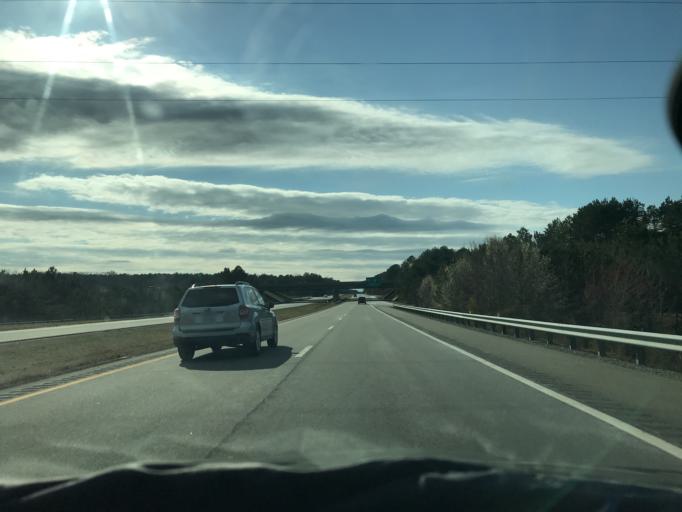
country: US
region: Virginia
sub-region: Chesterfield County
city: Brandermill
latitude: 37.4618
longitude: -77.6350
